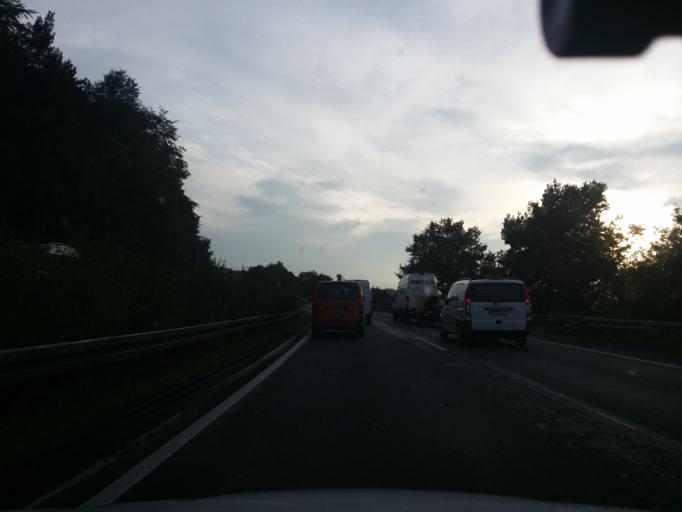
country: DE
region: Hesse
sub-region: Regierungsbezirk Kassel
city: Bad Hersfeld
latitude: 50.8625
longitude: 9.7756
